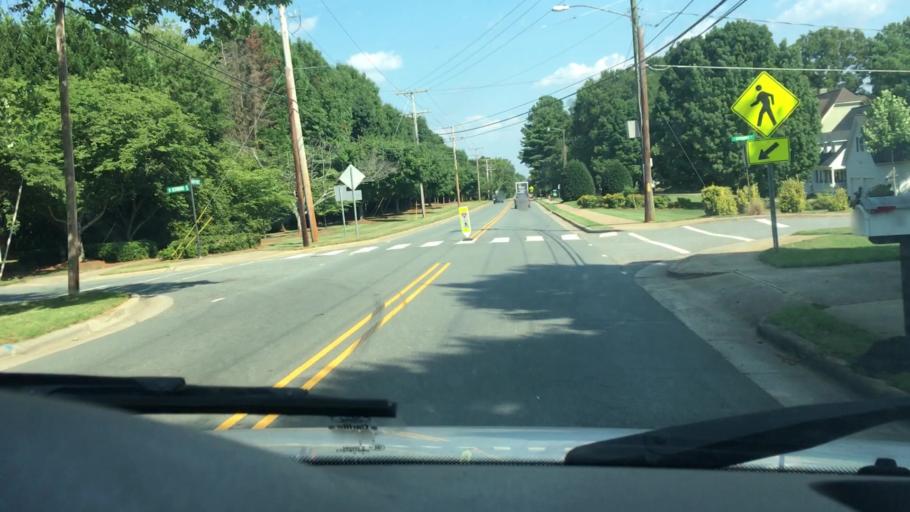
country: US
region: North Carolina
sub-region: Gaston County
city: Davidson
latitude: 35.4913
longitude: -80.8316
